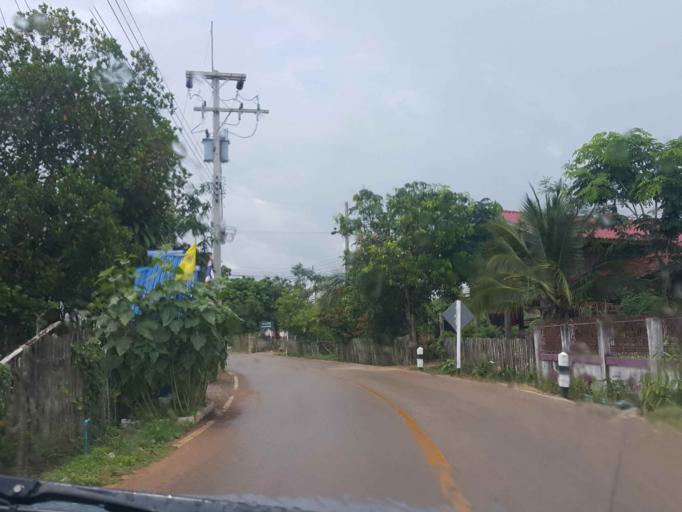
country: TH
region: Phayao
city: Dok Kham Tai
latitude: 19.0591
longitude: 100.0339
